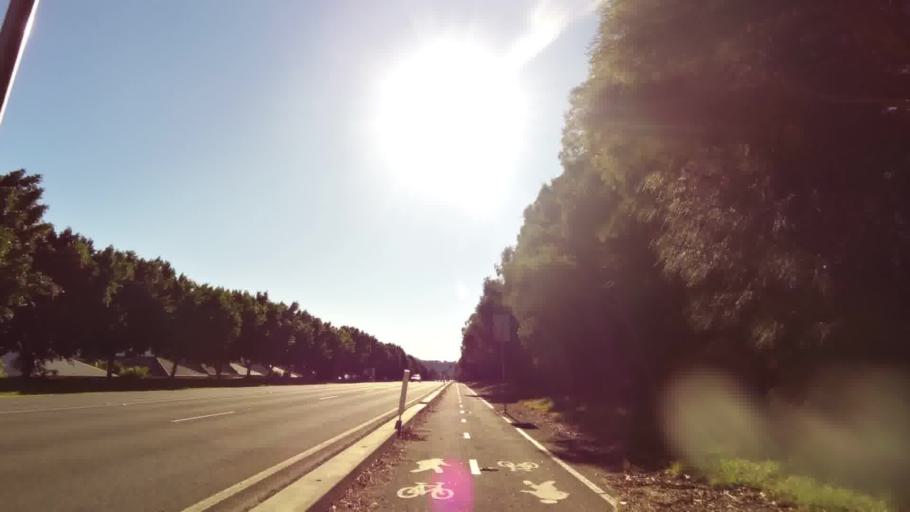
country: AU
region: New South Wales
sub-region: Wollongong
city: Koonawarra
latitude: -34.4880
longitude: 150.7983
